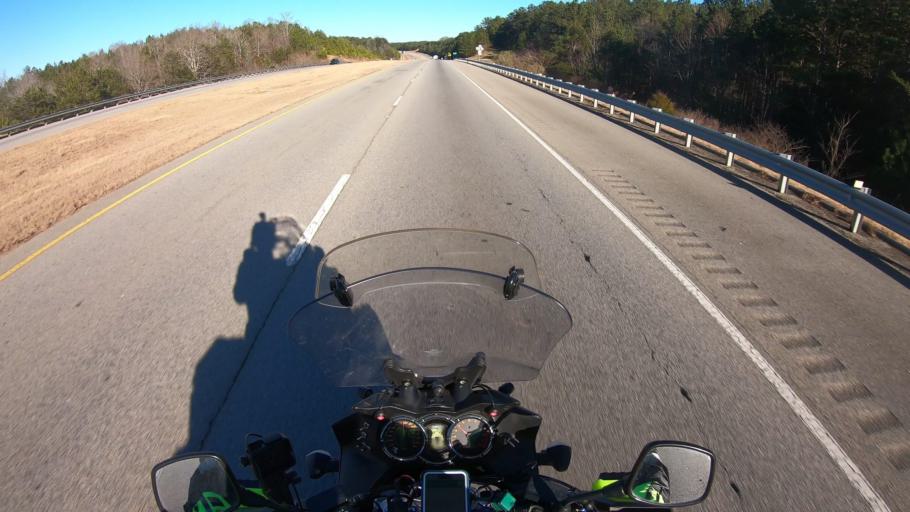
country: US
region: Georgia
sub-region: Polk County
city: Cedartown
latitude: 33.9926
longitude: -85.2401
